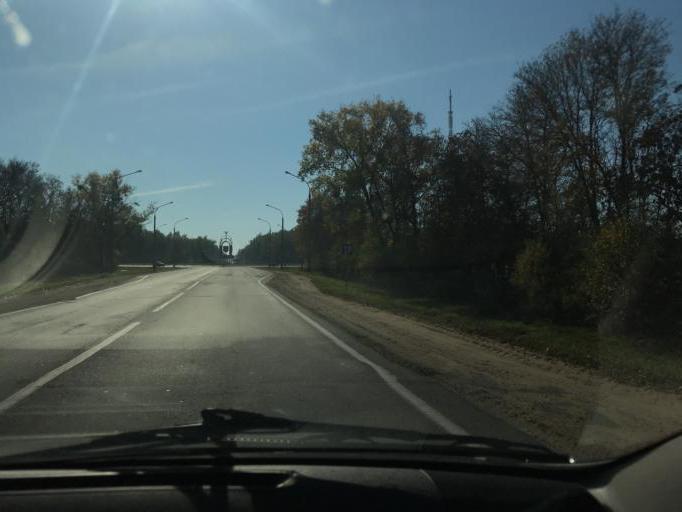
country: BY
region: Minsk
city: Starobin
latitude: 52.7842
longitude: 27.4645
